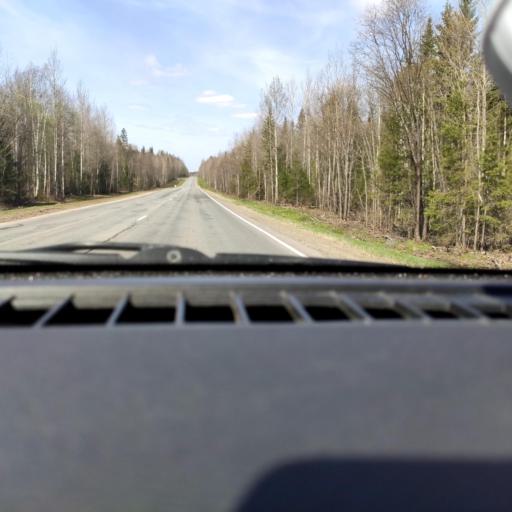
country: RU
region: Perm
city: Polazna
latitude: 58.2745
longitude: 56.1663
